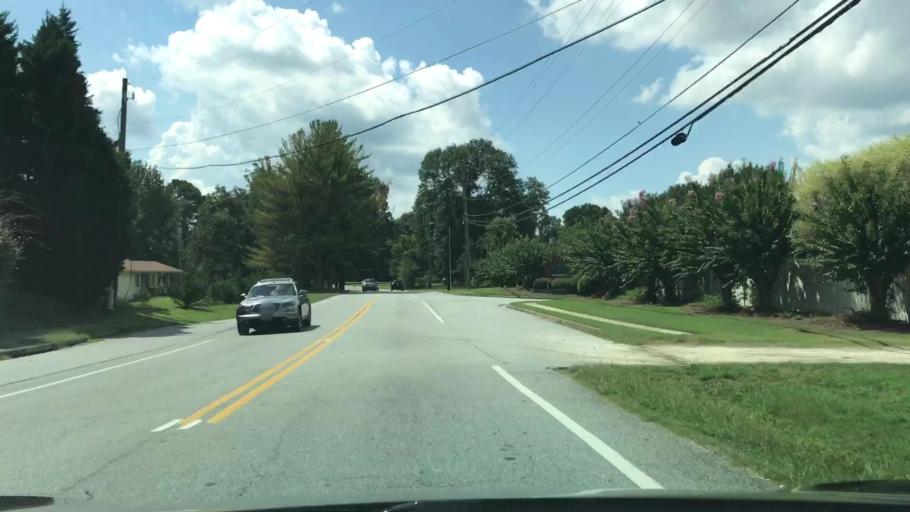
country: US
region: Georgia
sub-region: Gwinnett County
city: Lawrenceville
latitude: 33.9332
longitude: -84.0593
